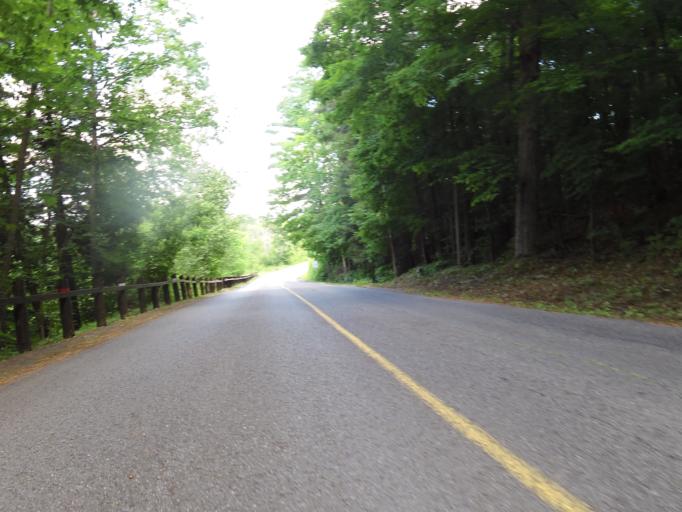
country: CA
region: Ontario
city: Arnprior
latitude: 45.4839
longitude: -76.2174
